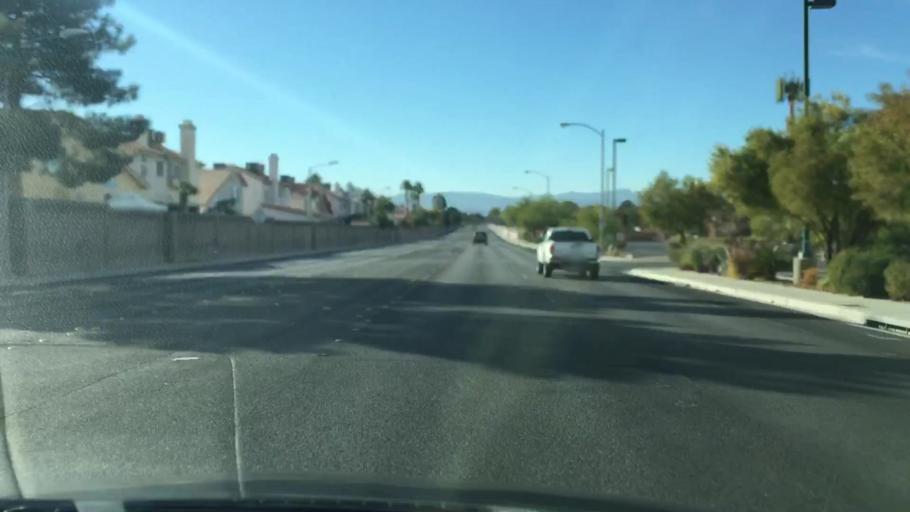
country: US
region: Nevada
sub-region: Clark County
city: Whitney
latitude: 36.0497
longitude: -115.1095
